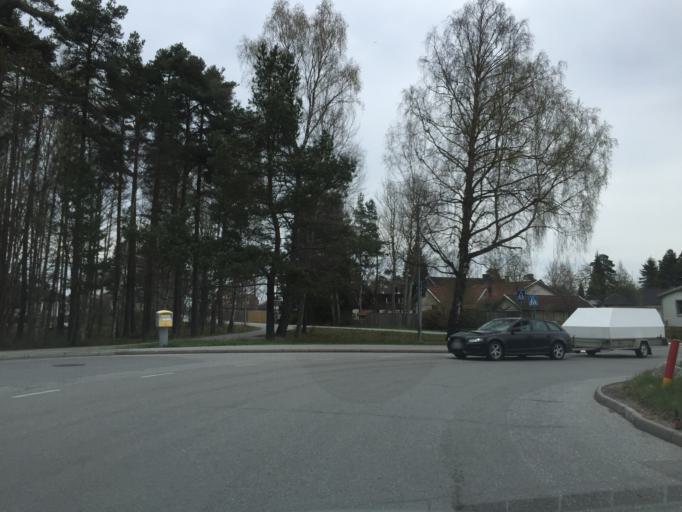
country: SE
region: OErebro
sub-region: Orebro Kommun
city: Orebro
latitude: 59.2452
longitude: 15.2449
